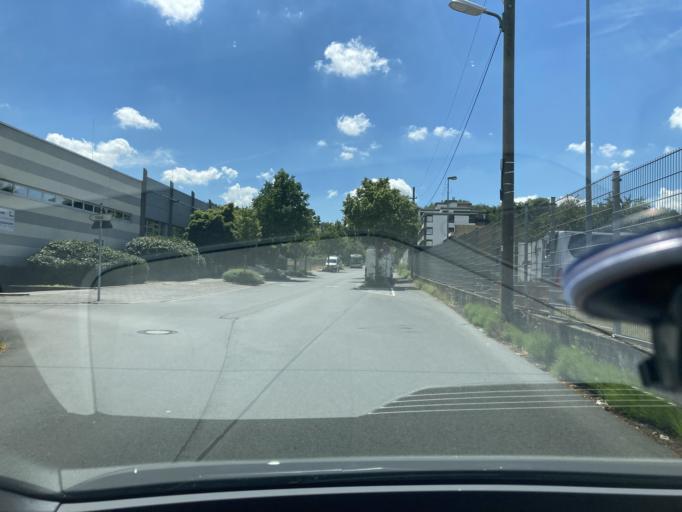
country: DE
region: Hesse
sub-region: Regierungsbezirk Darmstadt
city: Offenbach
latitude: 50.0815
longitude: 8.7464
